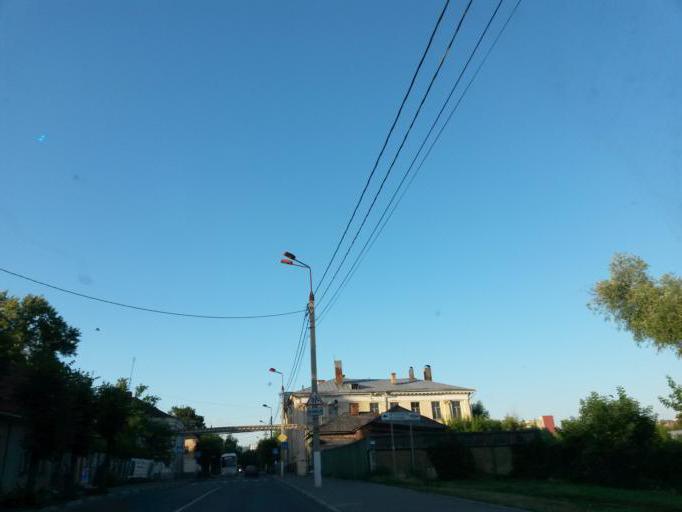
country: RU
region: Moskovskaya
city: Serpukhov
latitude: 54.9183
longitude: 37.4051
